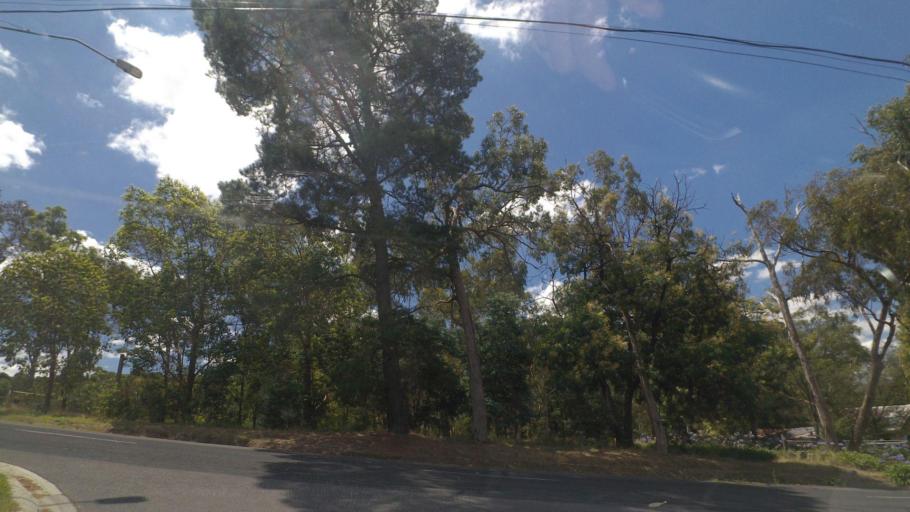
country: AU
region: Victoria
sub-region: Maroondah
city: Croydon Hills
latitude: -37.7623
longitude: 145.2818
